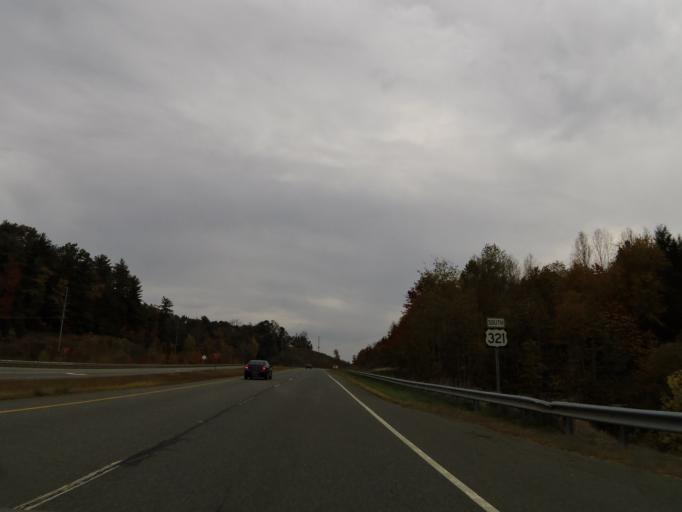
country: US
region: North Carolina
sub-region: Caldwell County
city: Lenoir
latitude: 36.0048
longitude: -81.5693
